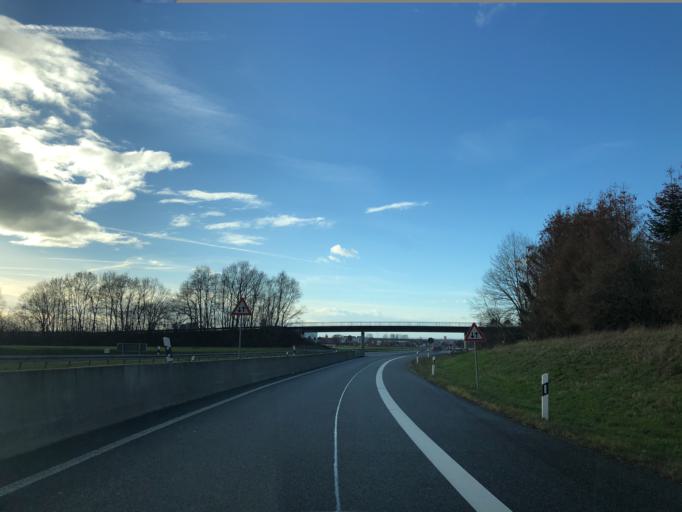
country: DE
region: Hesse
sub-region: Regierungsbezirk Darmstadt
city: Egelsbach
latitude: 49.9638
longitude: 8.6867
